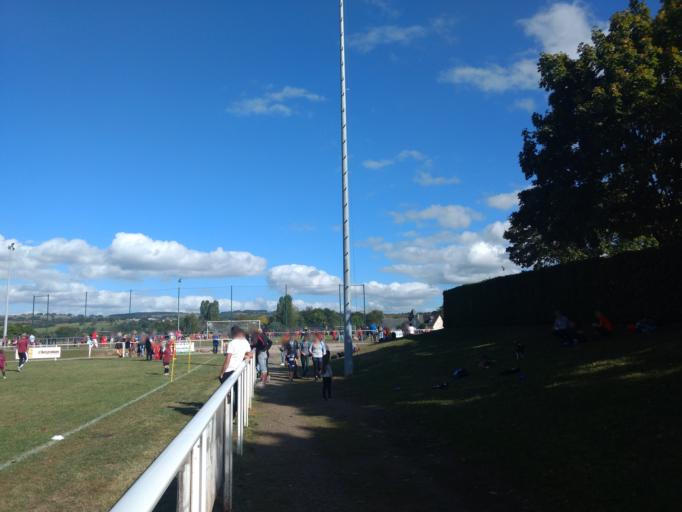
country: FR
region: Midi-Pyrenees
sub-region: Departement de l'Aveyron
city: Colombies
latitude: 44.4069
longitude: 2.2931
